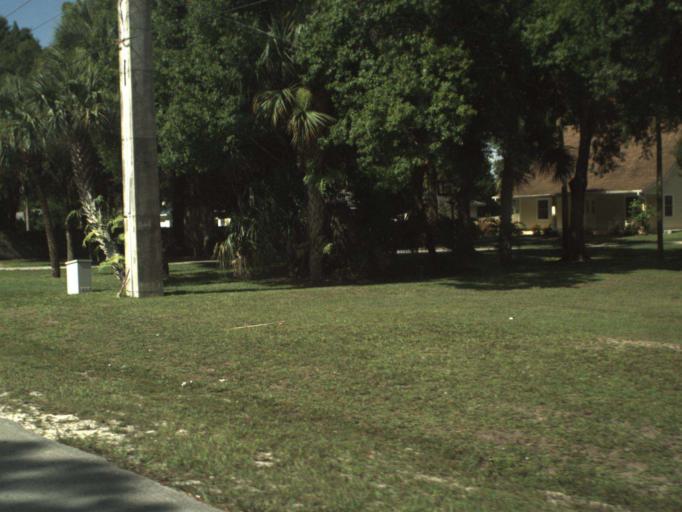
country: US
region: Florida
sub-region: Indian River County
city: Gifford
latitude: 27.6630
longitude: -80.4464
